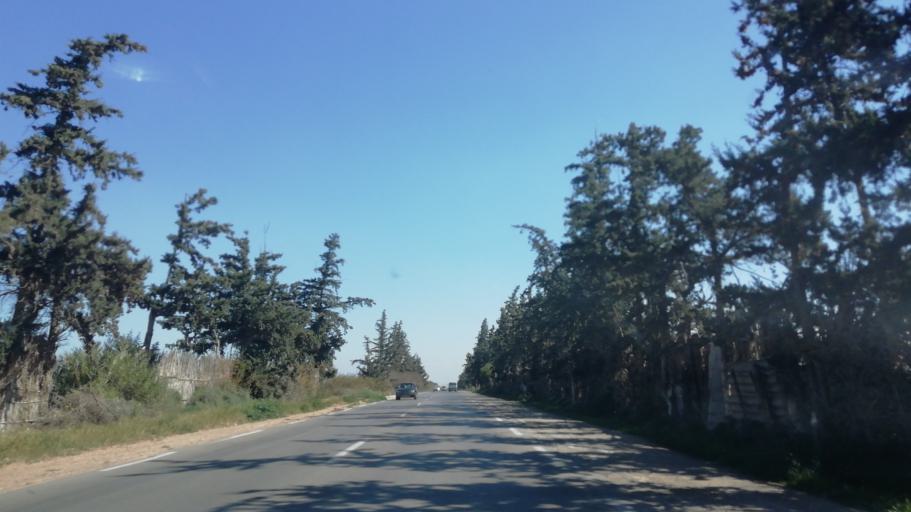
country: DZ
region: Mascara
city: Sig
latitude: 35.5676
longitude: -0.0643
